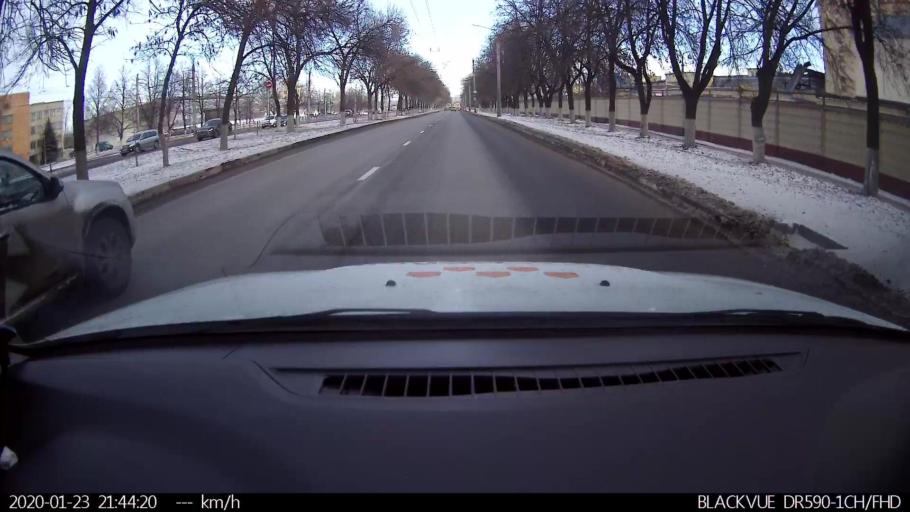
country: RU
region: Nizjnij Novgorod
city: Nizhniy Novgorod
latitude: 56.2554
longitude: 43.8956
